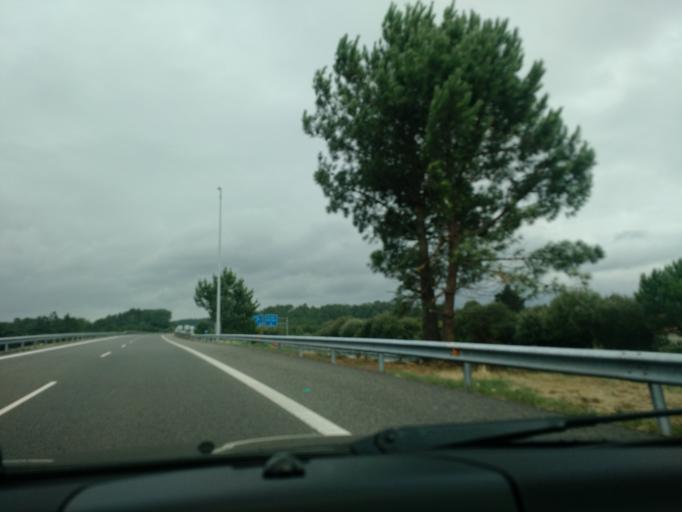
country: ES
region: Galicia
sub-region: Provincia da Coruna
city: Betanzos
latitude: 43.2757
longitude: -8.2602
